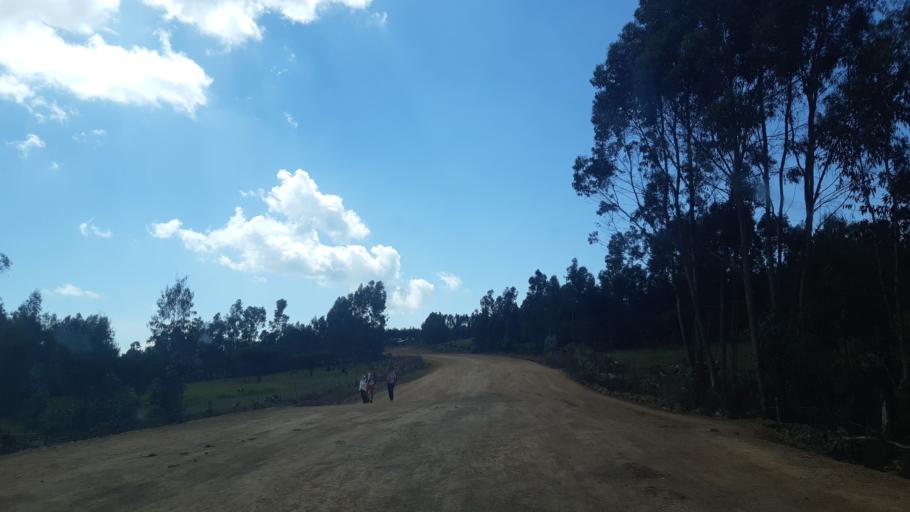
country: ET
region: Amhara
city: Dabat
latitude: 13.3655
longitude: 37.3835
